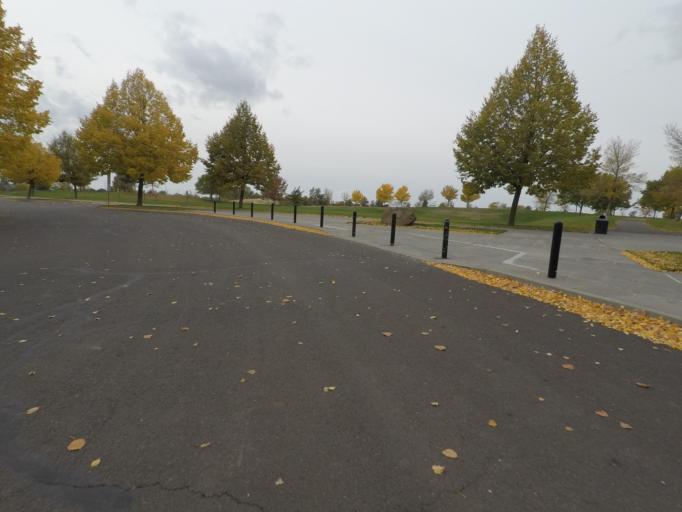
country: US
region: Washington
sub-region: Walla Walla County
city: Walla Walla East
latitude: 46.0728
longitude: -118.2894
